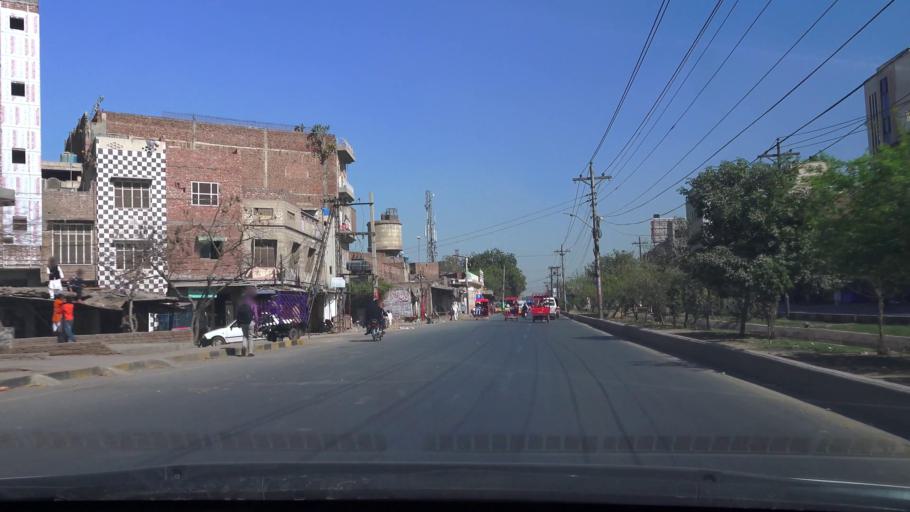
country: PK
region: Punjab
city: Faisalabad
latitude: 31.4131
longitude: 73.0677
